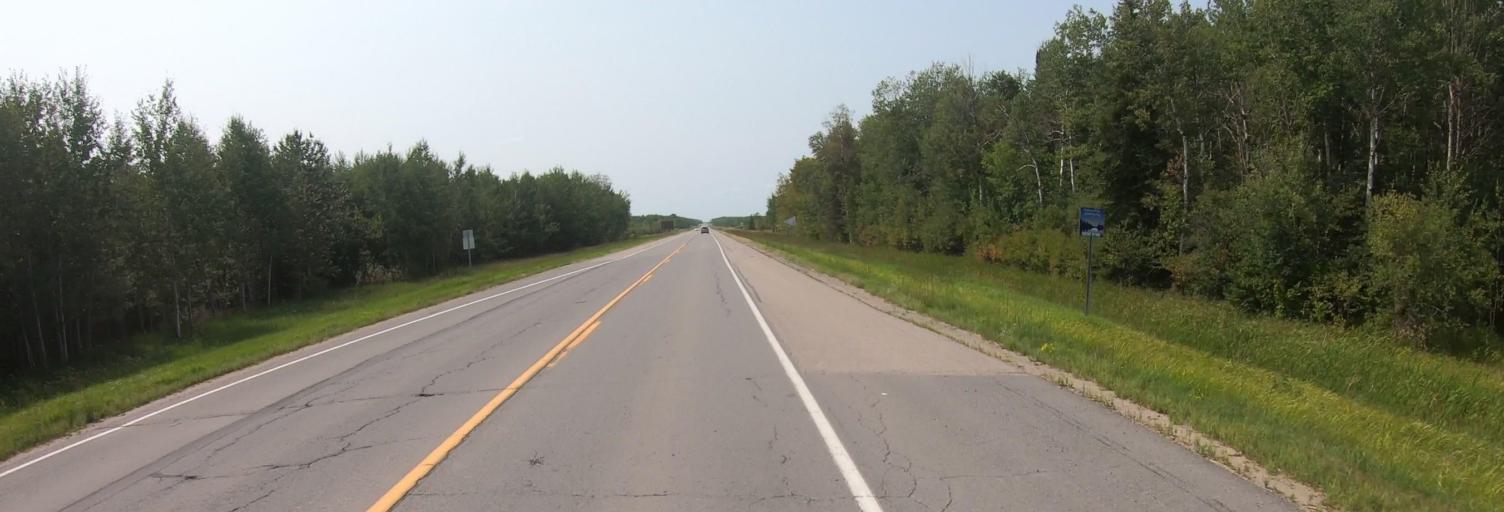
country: US
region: Minnesota
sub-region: Koochiching County
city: International Falls
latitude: 48.5533
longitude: -93.4445
